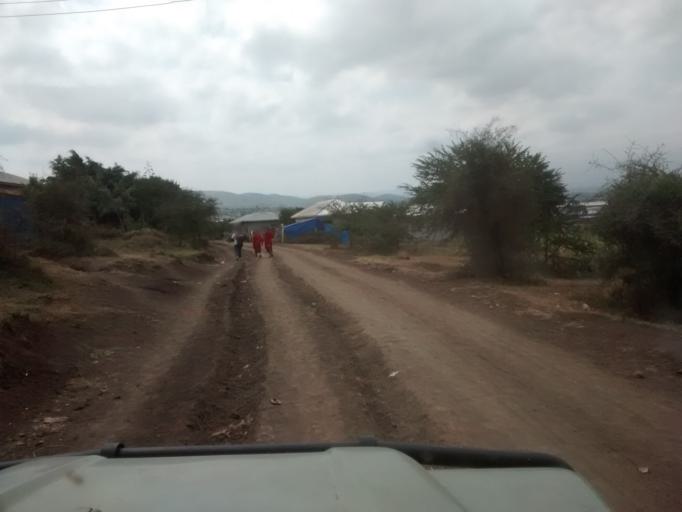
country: TZ
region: Arusha
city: Arusha
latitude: -3.3905
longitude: 36.5913
